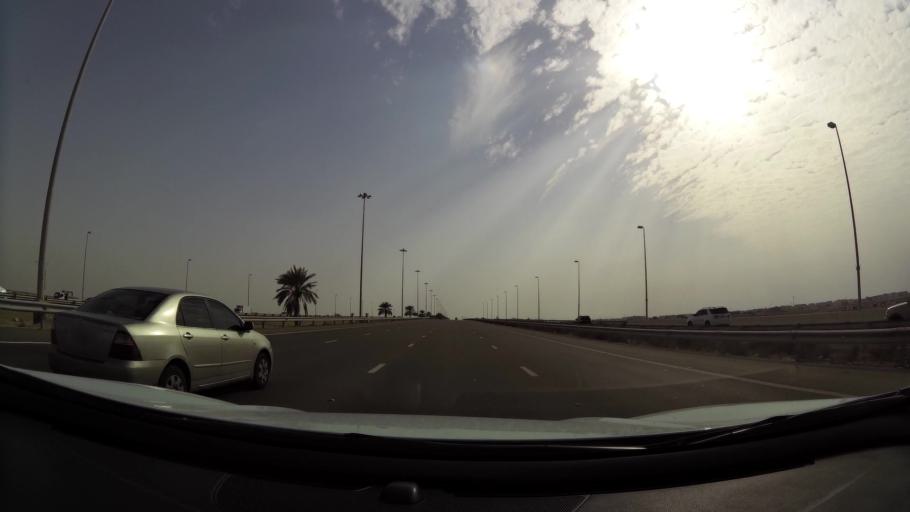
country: AE
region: Abu Dhabi
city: Abu Dhabi
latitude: 24.4006
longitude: 54.6689
